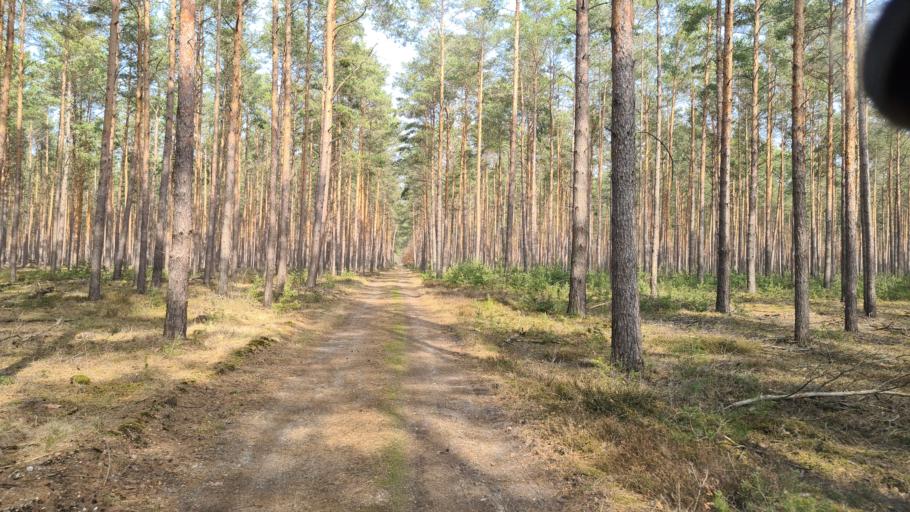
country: DE
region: Brandenburg
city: Trobitz
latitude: 51.6495
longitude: 13.4574
